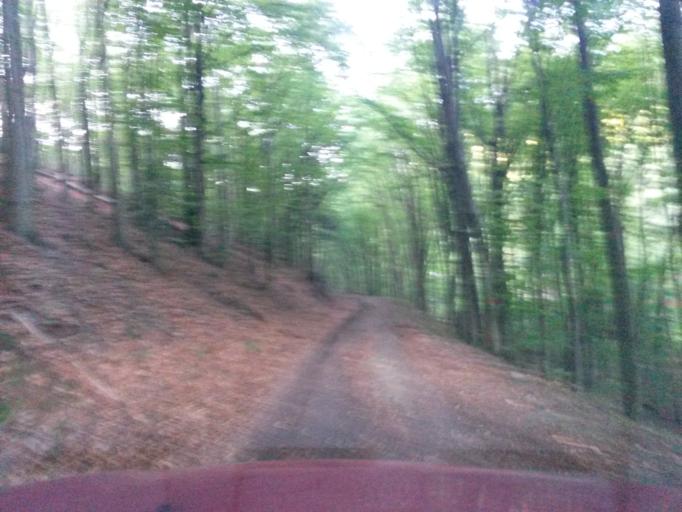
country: SK
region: Kosicky
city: Moldava nad Bodvou
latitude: 48.7349
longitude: 21.0639
